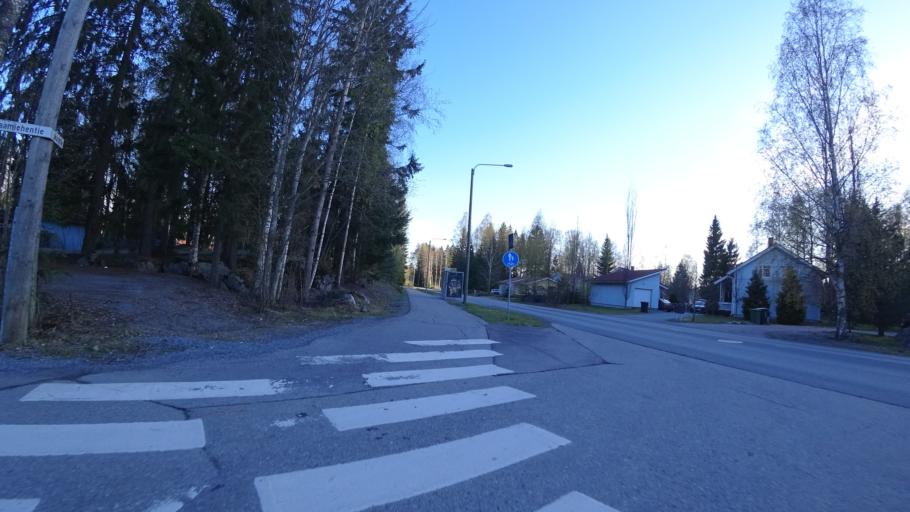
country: FI
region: Pirkanmaa
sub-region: Tampere
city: Yloejaervi
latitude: 61.5116
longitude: 23.5953
